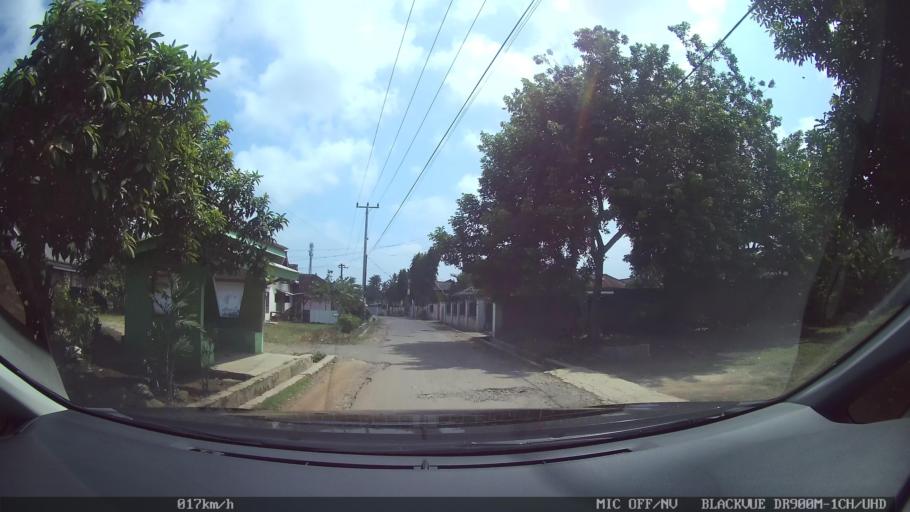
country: ID
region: Lampung
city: Kedaton
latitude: -5.3516
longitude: 105.2882
